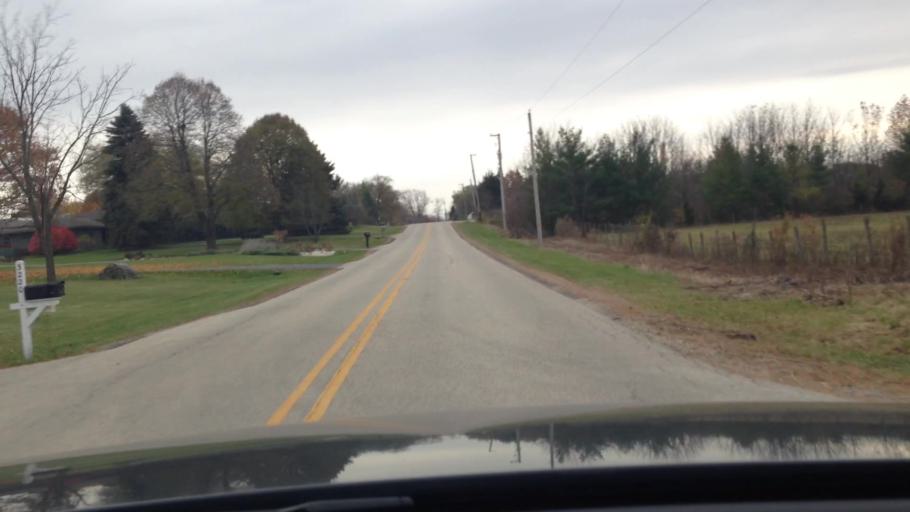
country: US
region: Illinois
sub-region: McHenry County
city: Woodstock
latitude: 42.2811
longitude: -88.4770
